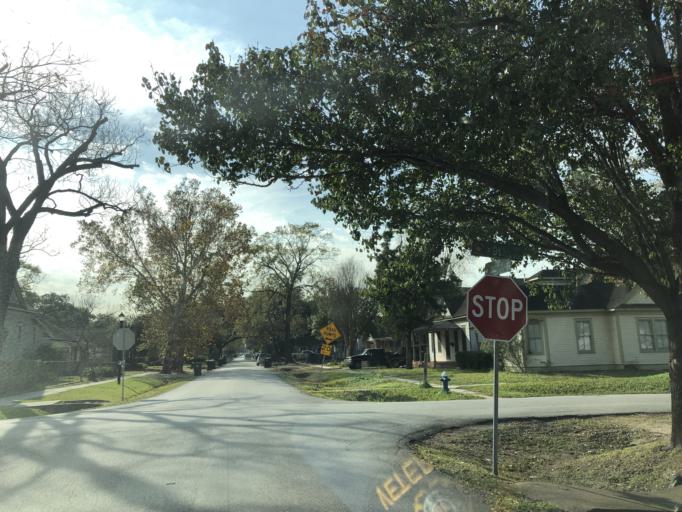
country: US
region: Texas
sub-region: Harris County
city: Houston
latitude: 29.7873
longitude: -95.3942
